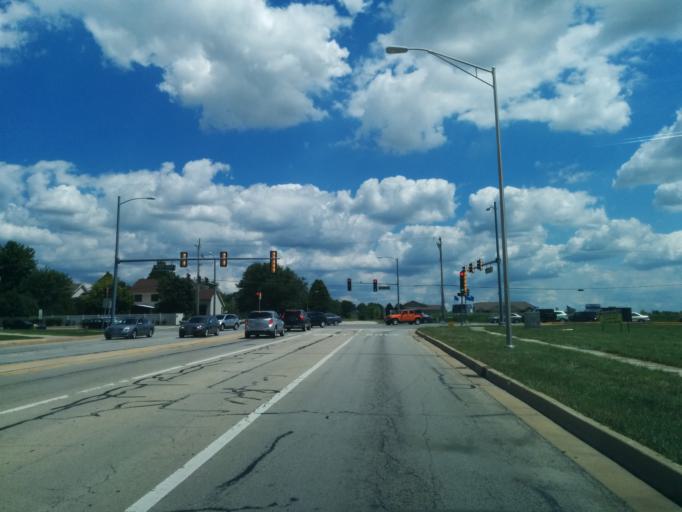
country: US
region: Illinois
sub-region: Will County
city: Romeoville
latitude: 41.6824
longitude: -88.1267
